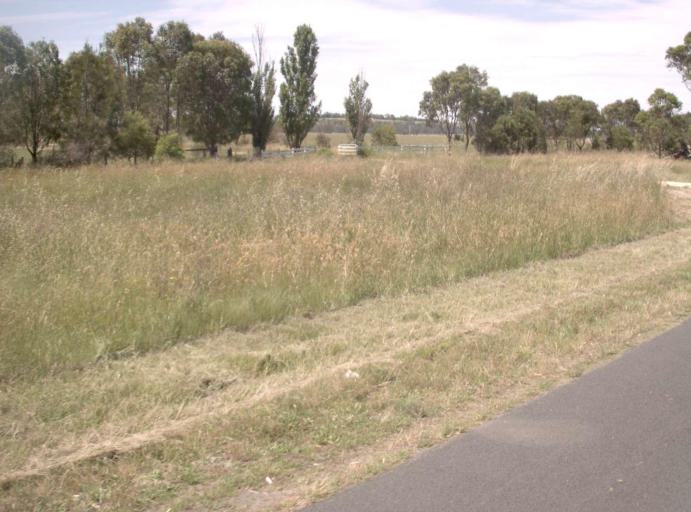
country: AU
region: Victoria
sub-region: Wellington
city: Heyfield
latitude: -38.1589
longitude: 146.7310
